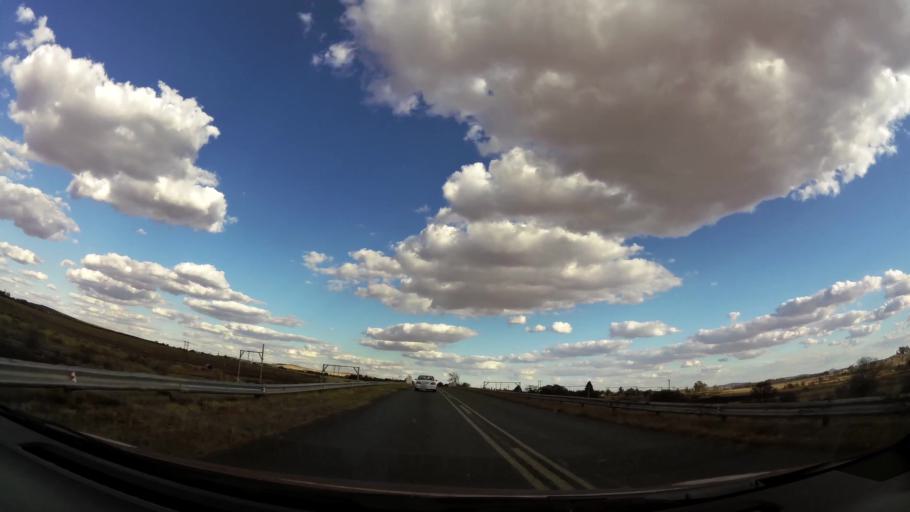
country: ZA
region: North-West
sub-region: Dr Kenneth Kaunda District Municipality
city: Potchefstroom
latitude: -26.6194
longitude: 27.1101
